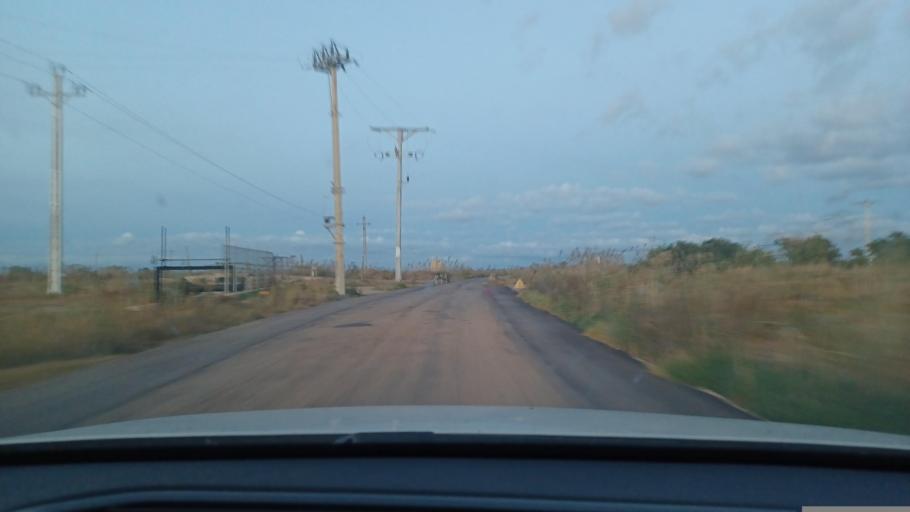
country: ES
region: Catalonia
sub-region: Provincia de Tarragona
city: Deltebre
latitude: 40.6492
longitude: 0.7601
